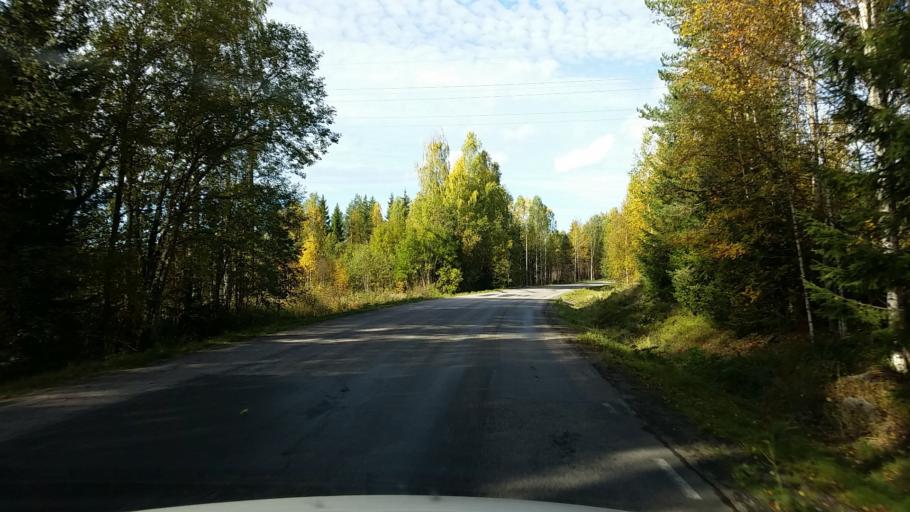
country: SE
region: Gaevleborg
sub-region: Ljusdals Kommun
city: Ljusdal
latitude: 61.8039
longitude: 16.1623
